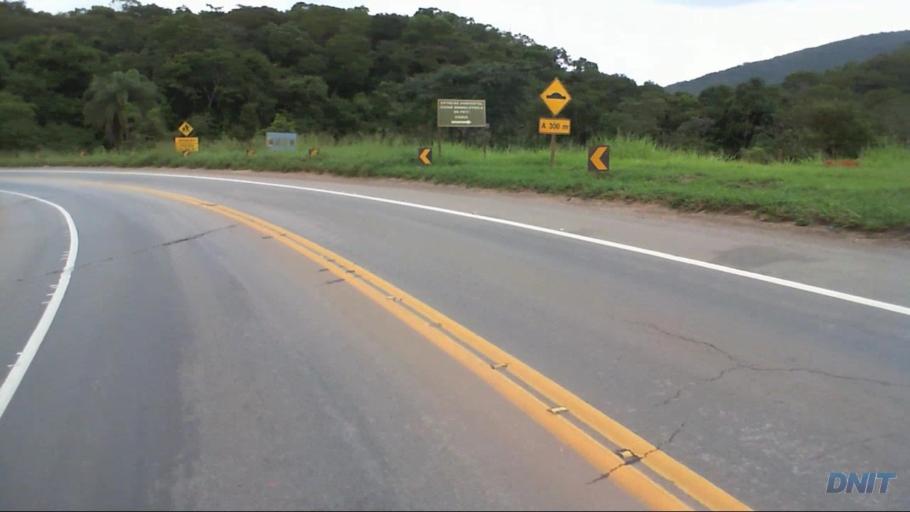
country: BR
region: Minas Gerais
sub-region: Barao De Cocais
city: Barao de Cocais
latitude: -19.8343
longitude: -43.3509
